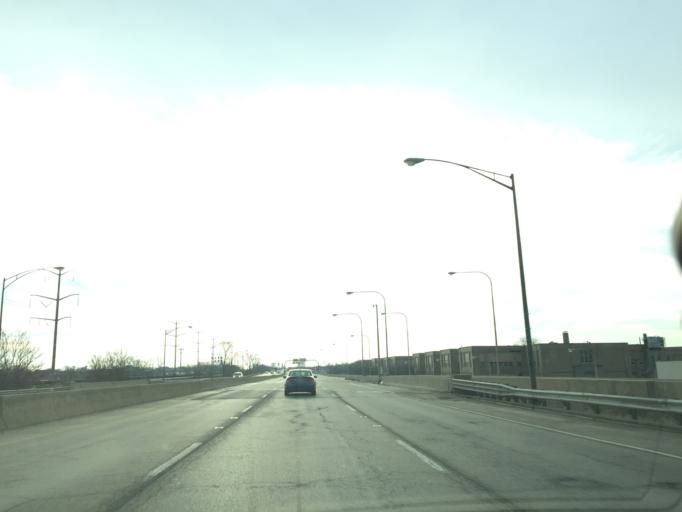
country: US
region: Indiana
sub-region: Lake County
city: Whiting
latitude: 41.7412
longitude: -87.5740
